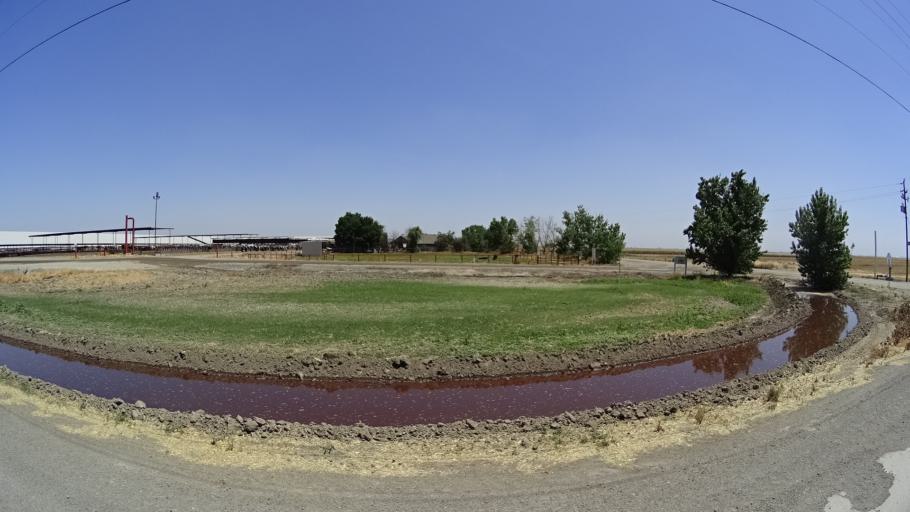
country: US
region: California
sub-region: Kings County
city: Home Garden
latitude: 36.1970
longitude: -119.6460
